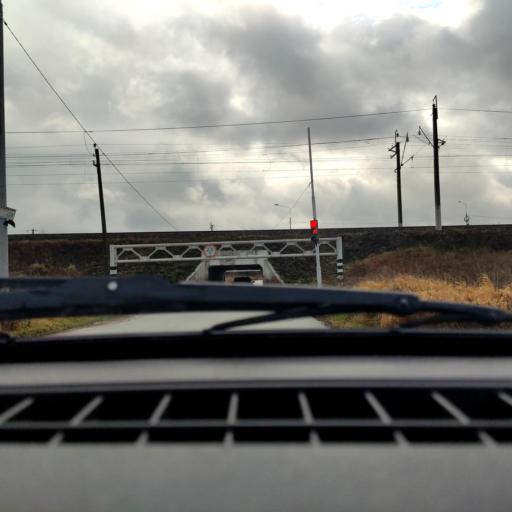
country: RU
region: Bashkortostan
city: Kabakovo
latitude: 54.6405
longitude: 56.0780
